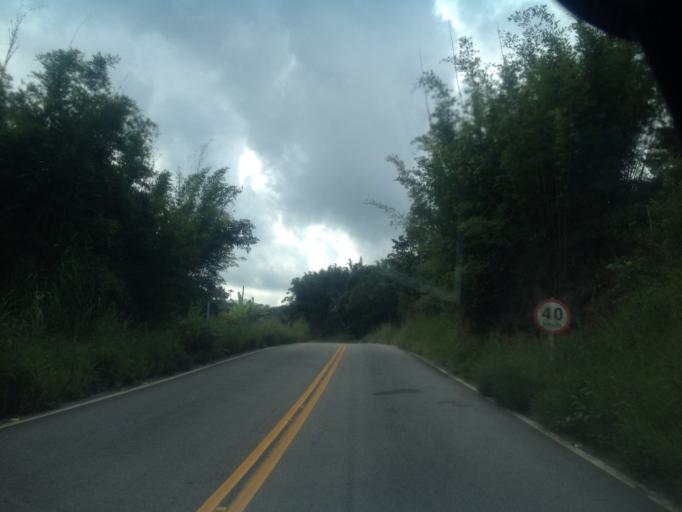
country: BR
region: Rio de Janeiro
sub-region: Quatis
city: Quatis
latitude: -22.3802
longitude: -44.2611
